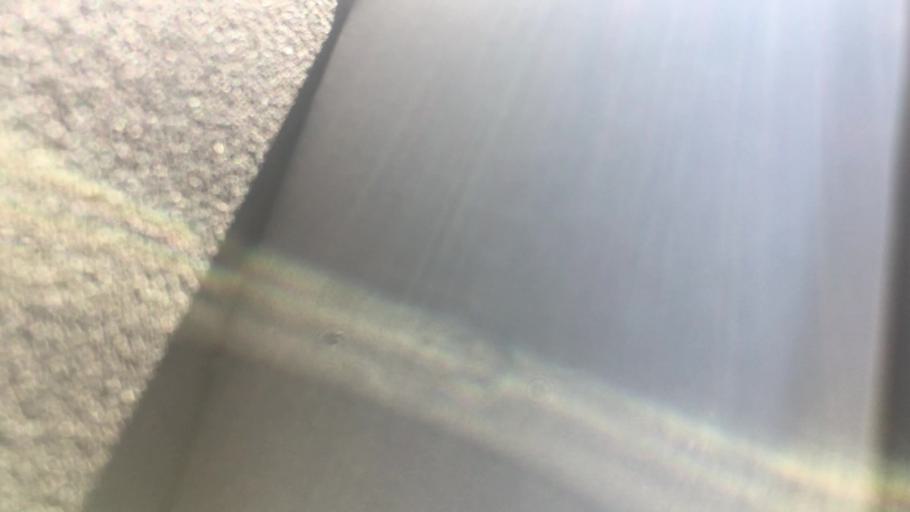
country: US
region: Maryland
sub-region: Worcester County
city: Pocomoke City
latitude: 38.0790
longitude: -75.5738
